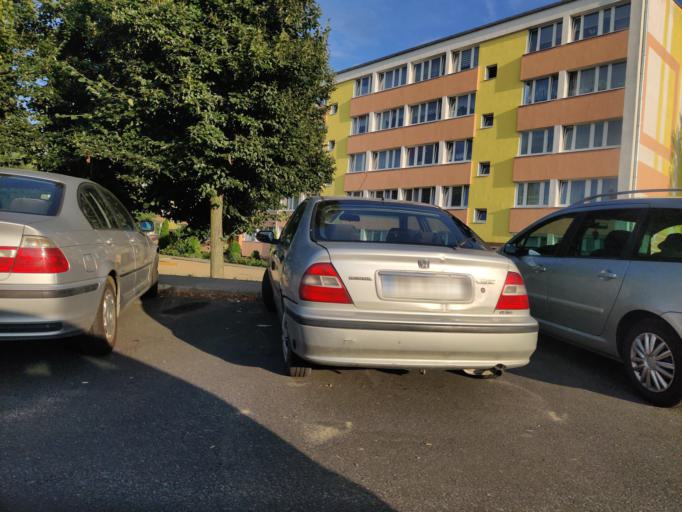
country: PL
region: Greater Poland Voivodeship
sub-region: Konin
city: Konin
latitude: 52.2313
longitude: 18.2760
